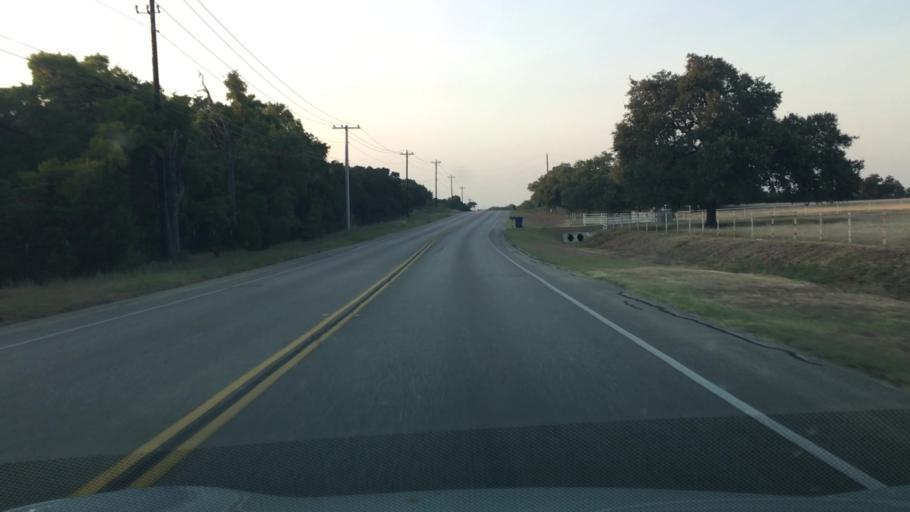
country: US
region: Texas
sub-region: Hays County
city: Dripping Springs
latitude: 30.1574
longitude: -98.0090
